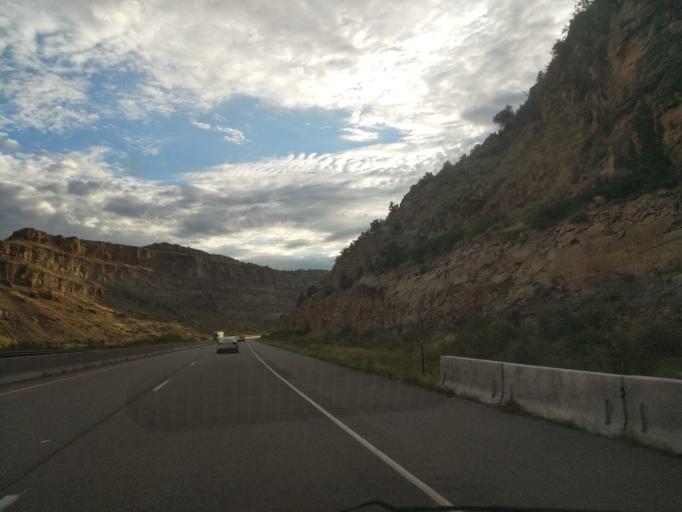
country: US
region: Colorado
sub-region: Mesa County
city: Palisade
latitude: 39.2351
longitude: -108.2710
